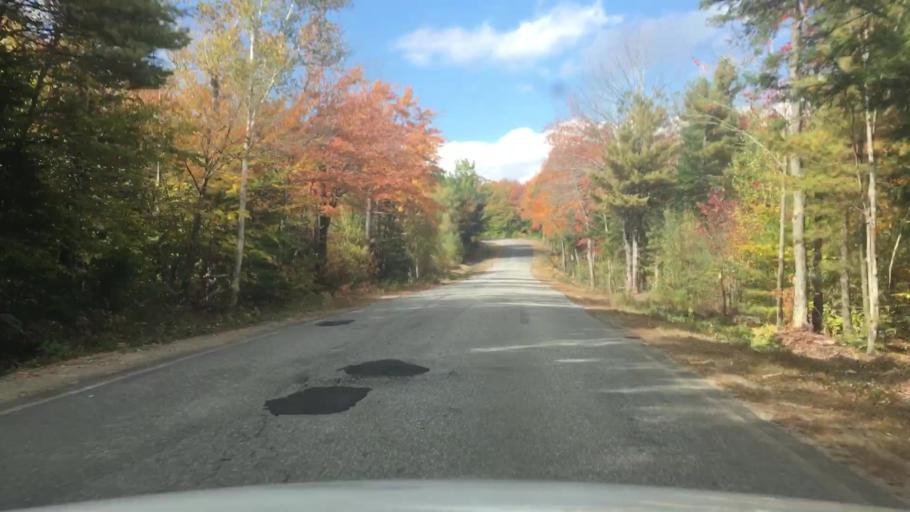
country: US
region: Maine
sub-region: Knox County
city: Washington
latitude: 44.3352
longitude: -69.3718
